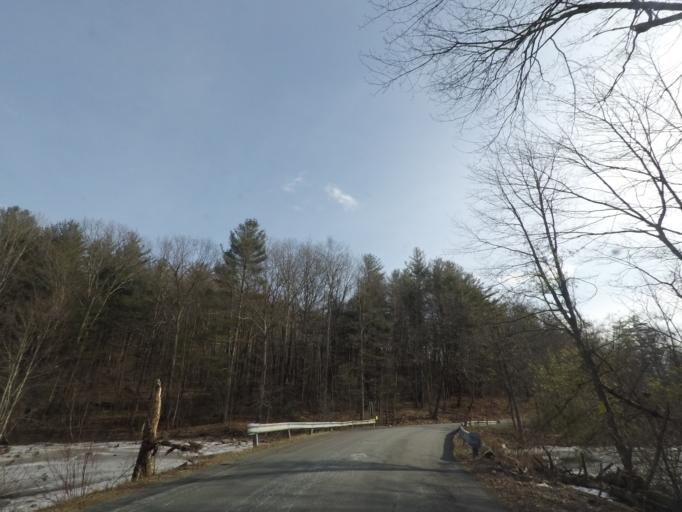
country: US
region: New York
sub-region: Rensselaer County
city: Nassau
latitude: 42.5187
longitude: -73.5641
